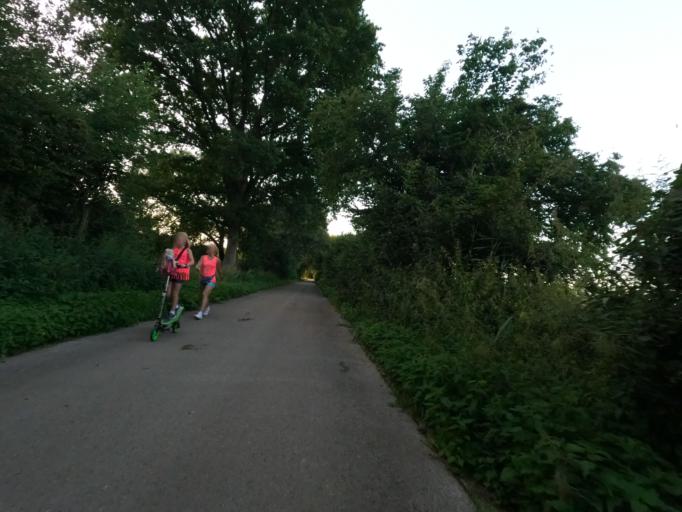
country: DE
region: North Rhine-Westphalia
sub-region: Regierungsbezirk Koln
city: Linnich
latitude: 51.0139
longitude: 6.2662
